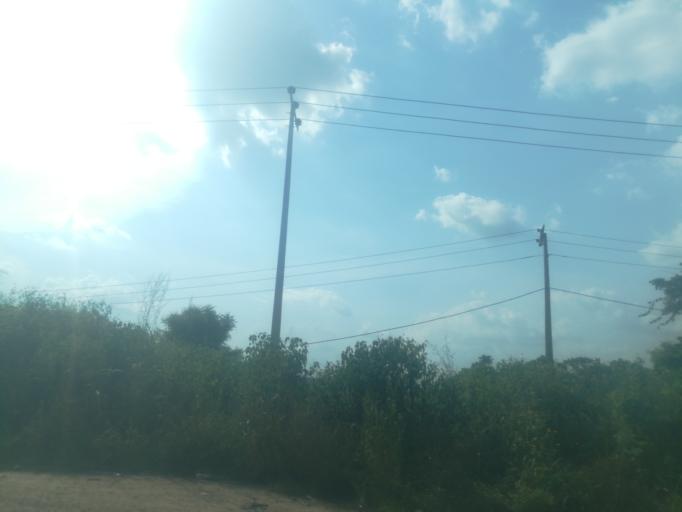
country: NG
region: Ogun
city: Abeokuta
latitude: 7.1000
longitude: 3.2965
